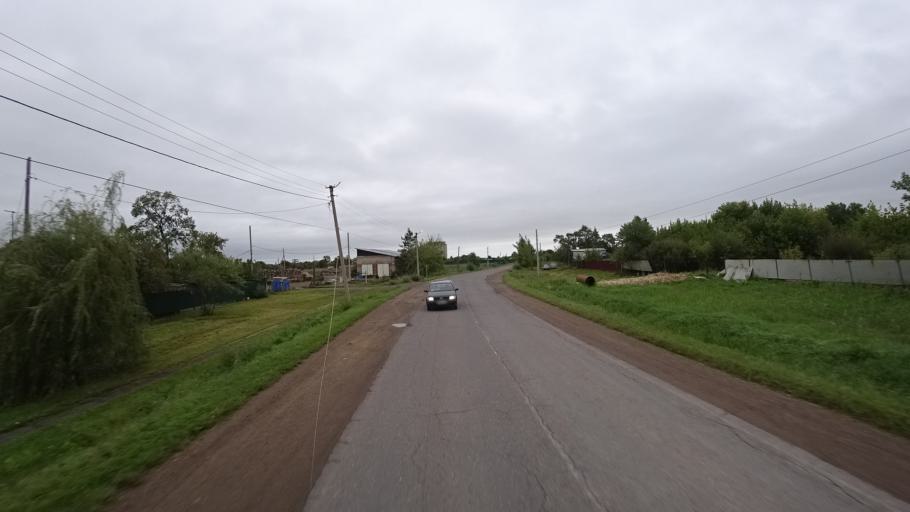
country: RU
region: Primorskiy
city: Chernigovka
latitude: 44.3417
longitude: 132.5394
